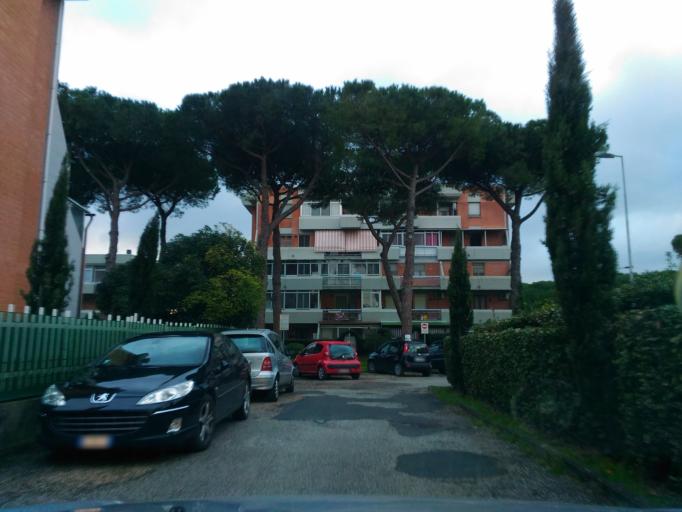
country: IT
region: Tuscany
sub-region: Provincia di Livorno
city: Guasticce
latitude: 43.5921
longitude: 10.3566
